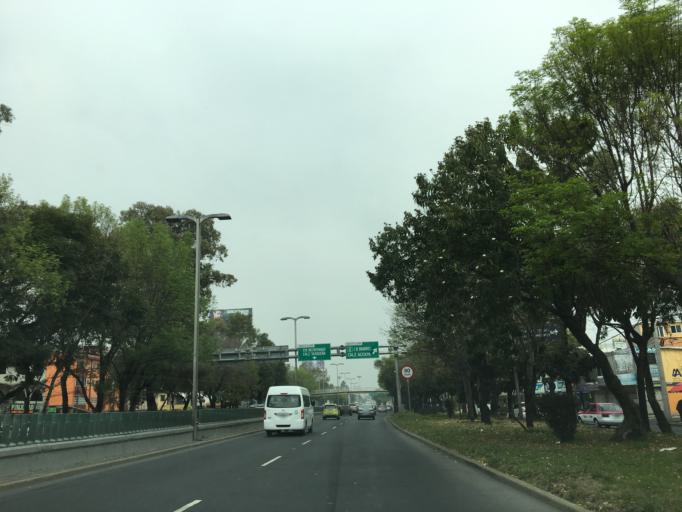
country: MX
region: Mexico City
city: Tlalpan
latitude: 19.2947
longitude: -99.1466
